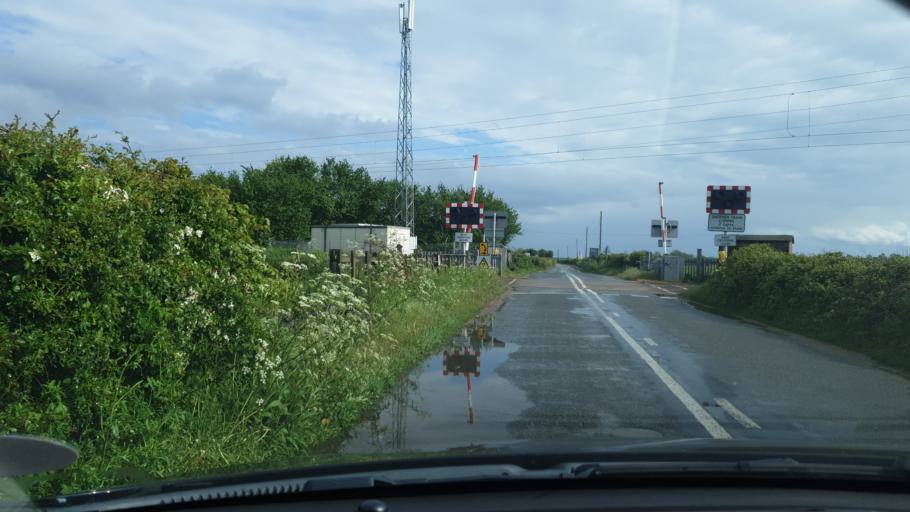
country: GB
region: England
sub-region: Essex
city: Great Bentley
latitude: 51.8495
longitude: 1.0452
